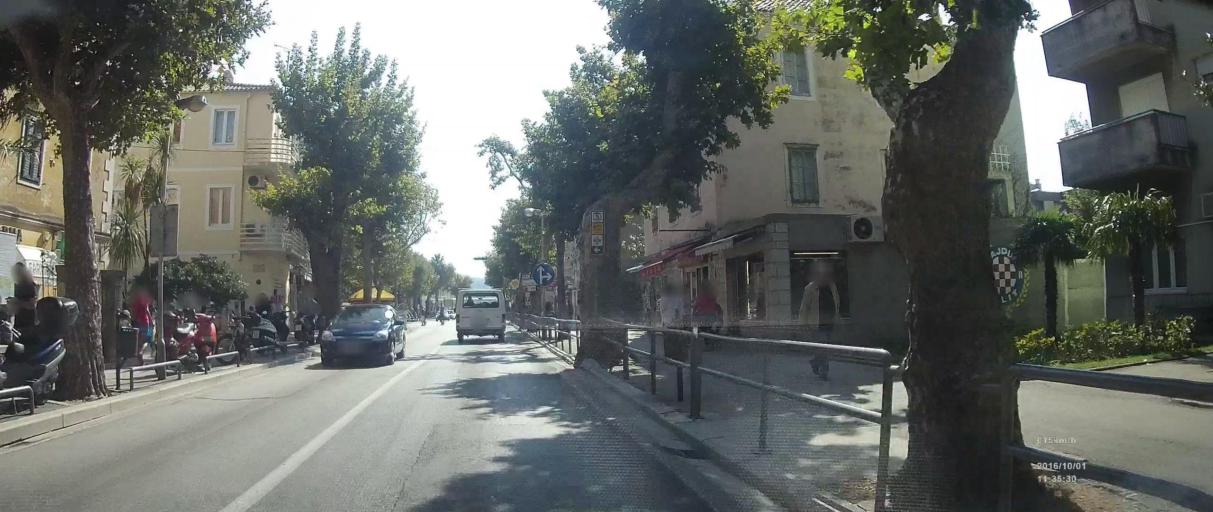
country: HR
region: Splitsko-Dalmatinska
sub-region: Grad Omis
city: Omis
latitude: 43.4439
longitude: 16.6924
